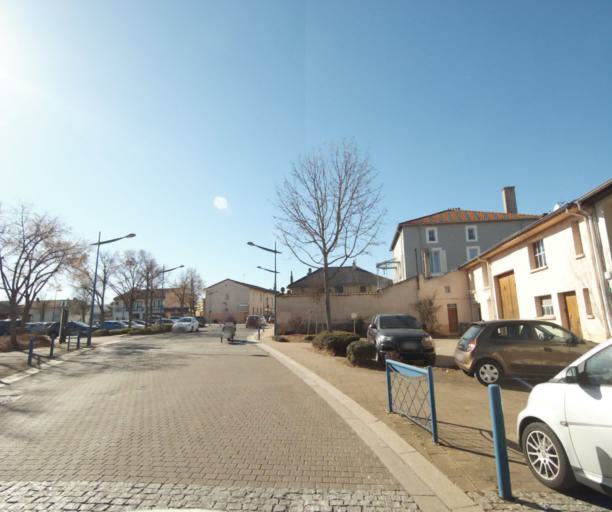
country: FR
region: Lorraine
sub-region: Departement de Meurthe-et-Moselle
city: Vandoeuvre-les-Nancy
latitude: 48.6532
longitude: 6.1943
